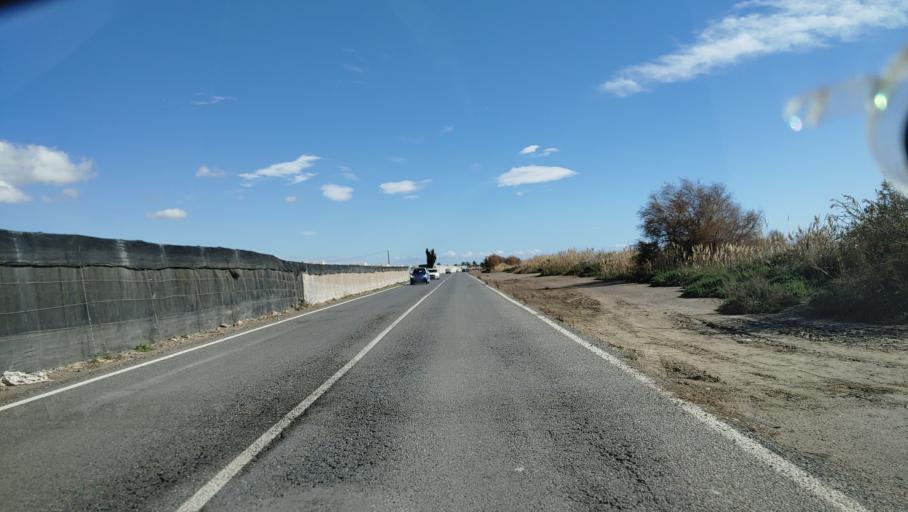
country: ES
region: Andalusia
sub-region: Provincia de Almeria
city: Roquetas de Mar
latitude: 36.7898
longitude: -2.5979
